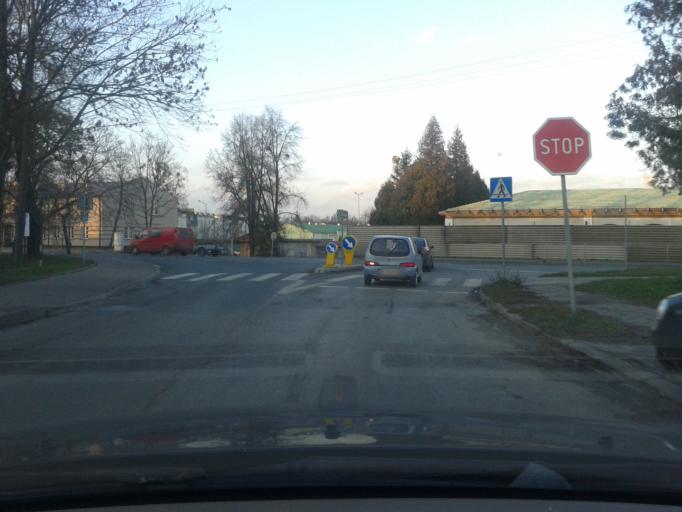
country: PL
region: Lublin Voivodeship
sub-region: Powiat opolski
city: Opole Lubelskie
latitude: 51.1462
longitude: 21.9766
